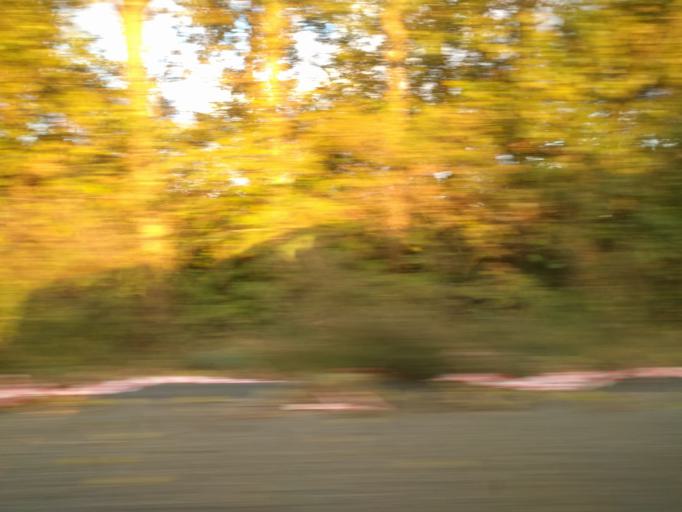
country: DK
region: South Denmark
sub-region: Nyborg Kommune
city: Nyborg
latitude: 55.3133
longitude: 10.8111
